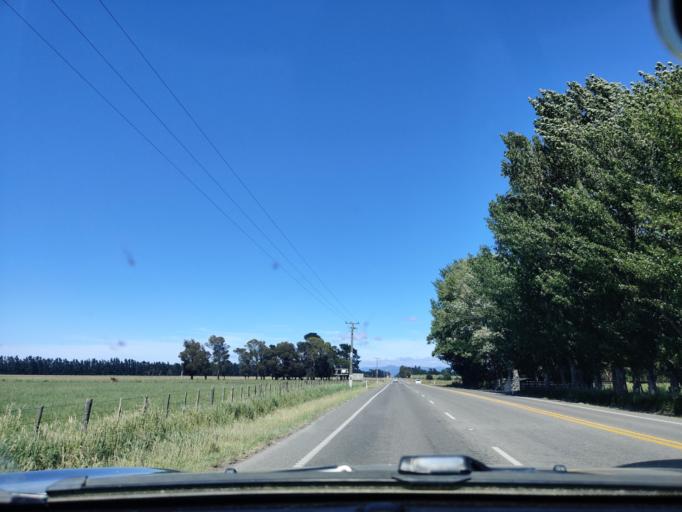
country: NZ
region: Wellington
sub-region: Masterton District
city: Masterton
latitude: -41.0947
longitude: 175.4383
